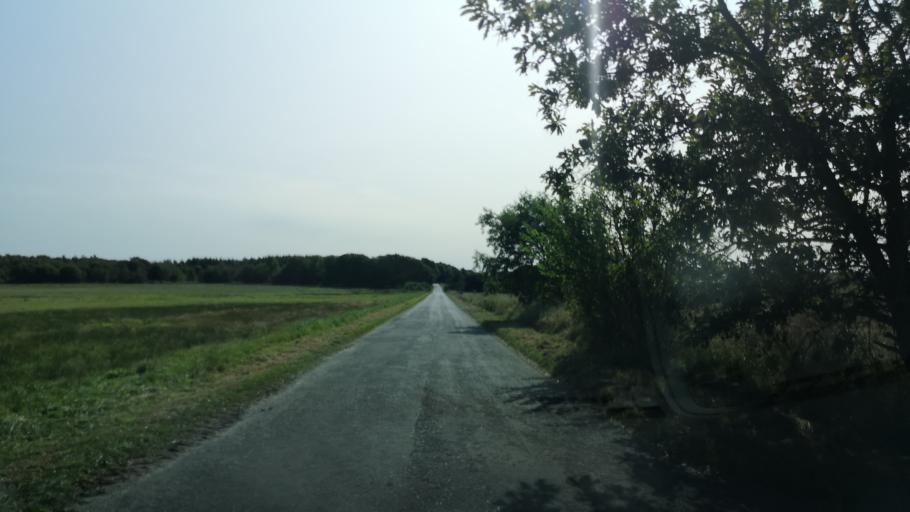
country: DK
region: Central Jutland
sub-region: Herning Kommune
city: Herning
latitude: 56.1737
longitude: 8.9537
